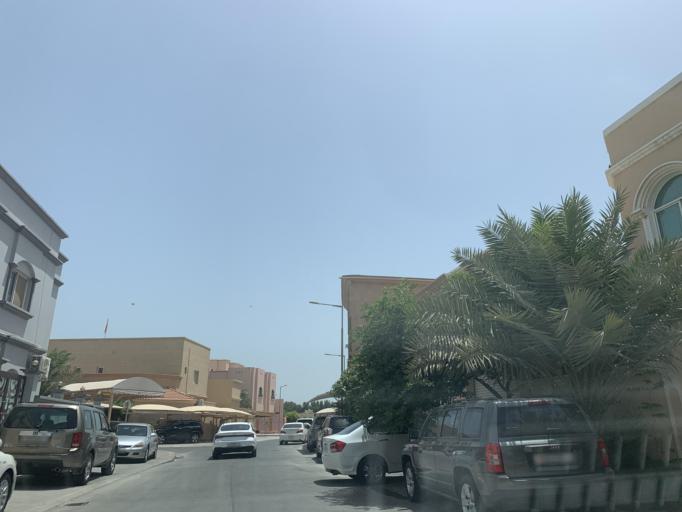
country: BH
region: Northern
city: Madinat `Isa
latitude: 26.1613
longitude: 50.5769
